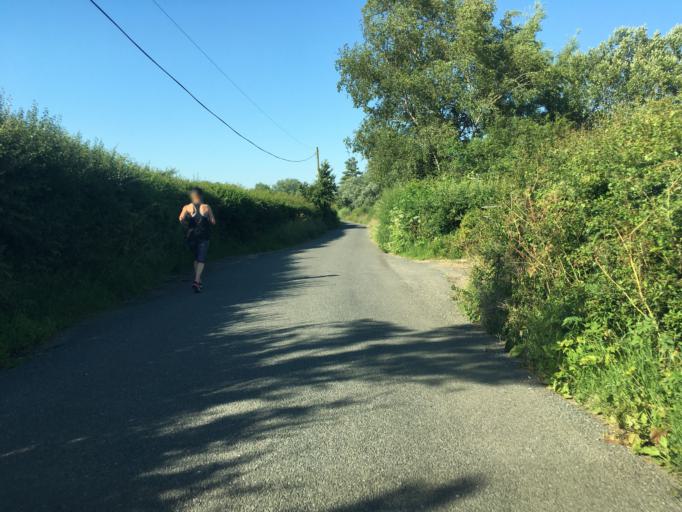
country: GB
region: England
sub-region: South Gloucestershire
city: Hinton
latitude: 51.4727
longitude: -2.3990
